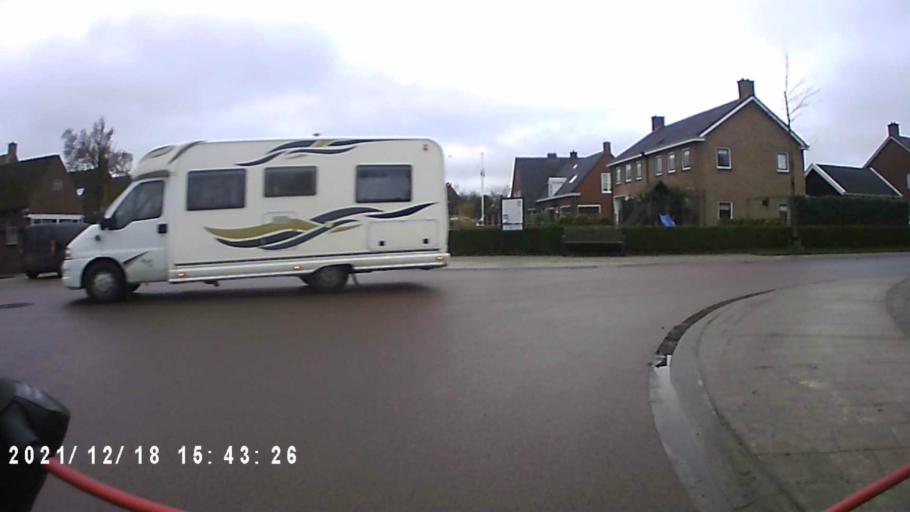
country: NL
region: Friesland
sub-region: Gemeente Dongeradeel
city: Anjum
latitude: 53.3316
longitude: 6.1001
